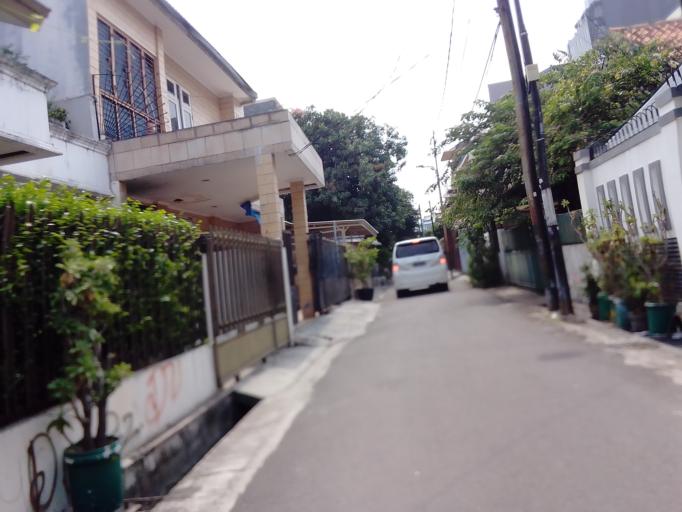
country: ID
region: Jakarta Raya
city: Jakarta
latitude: -6.1757
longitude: 106.8092
